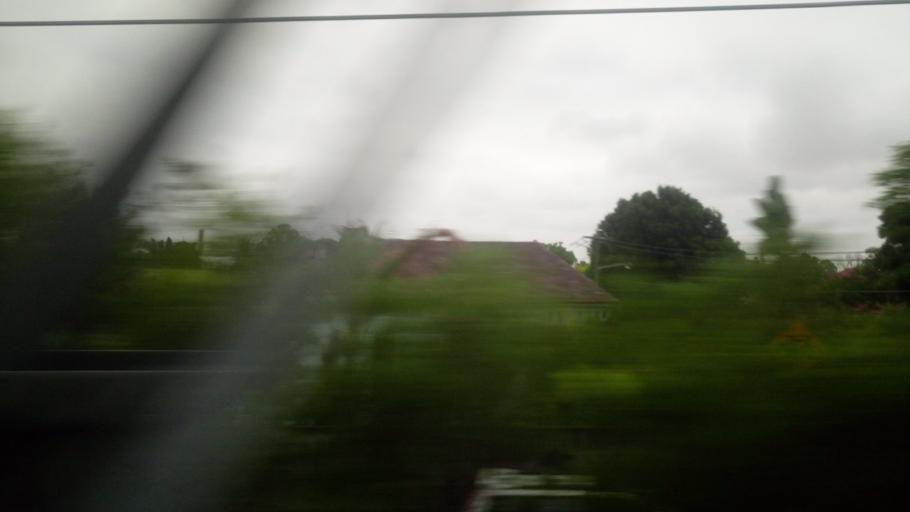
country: AU
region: New South Wales
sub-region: Ashfield
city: Croydon
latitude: -33.8787
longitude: 151.1097
